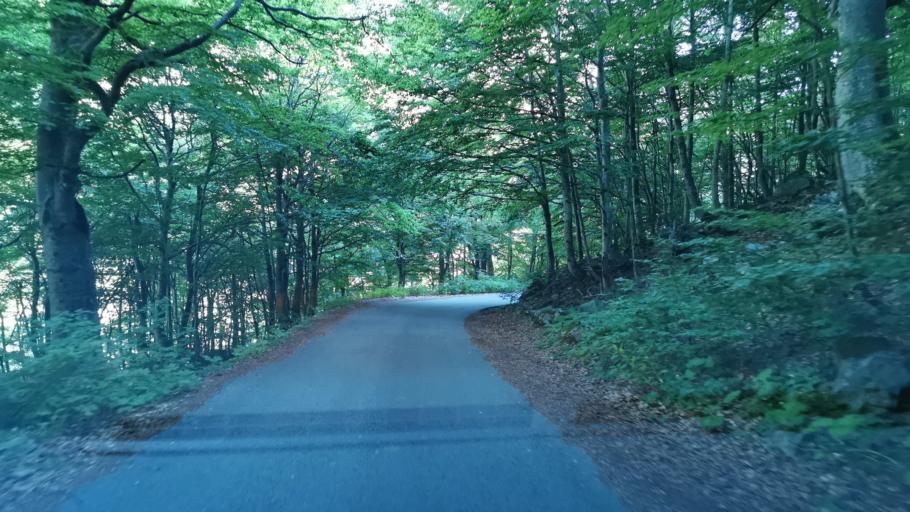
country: IT
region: Piedmont
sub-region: Provincia di Cuneo
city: Demonte
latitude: 44.2055
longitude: 7.2714
